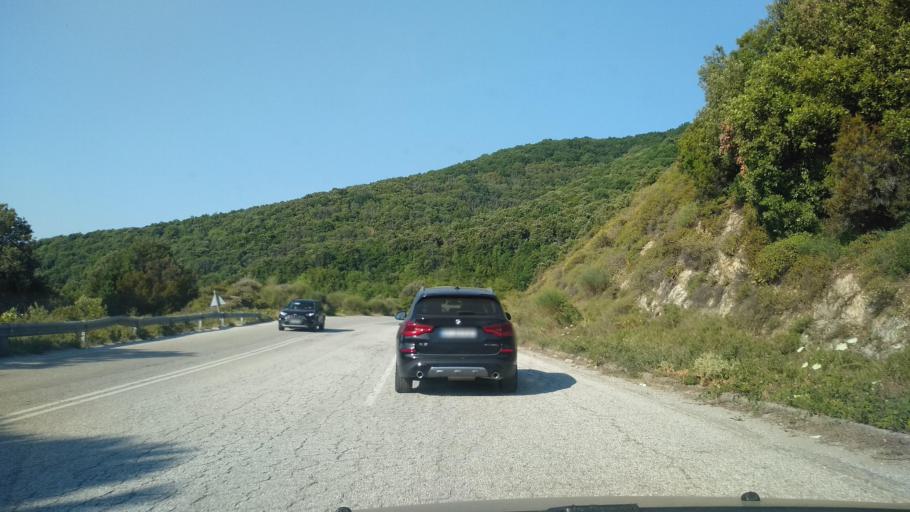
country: GR
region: Central Macedonia
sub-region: Nomos Chalkidikis
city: Stratonion
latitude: 40.5298
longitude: 23.8263
